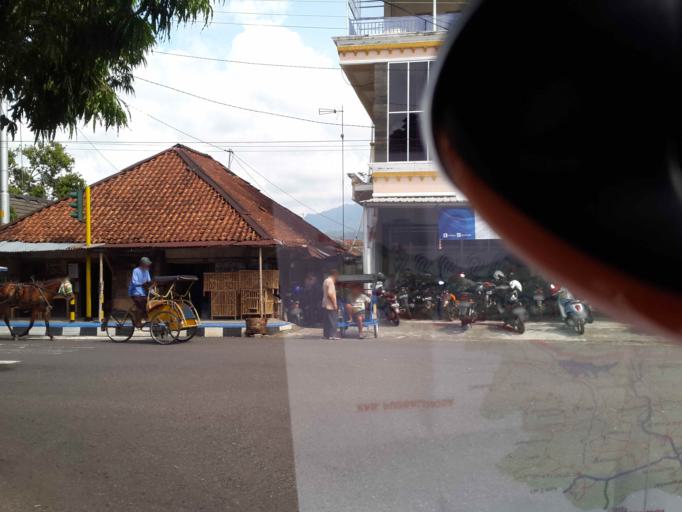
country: ID
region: Central Java
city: Wonosobo
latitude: -7.3929
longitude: 109.6959
